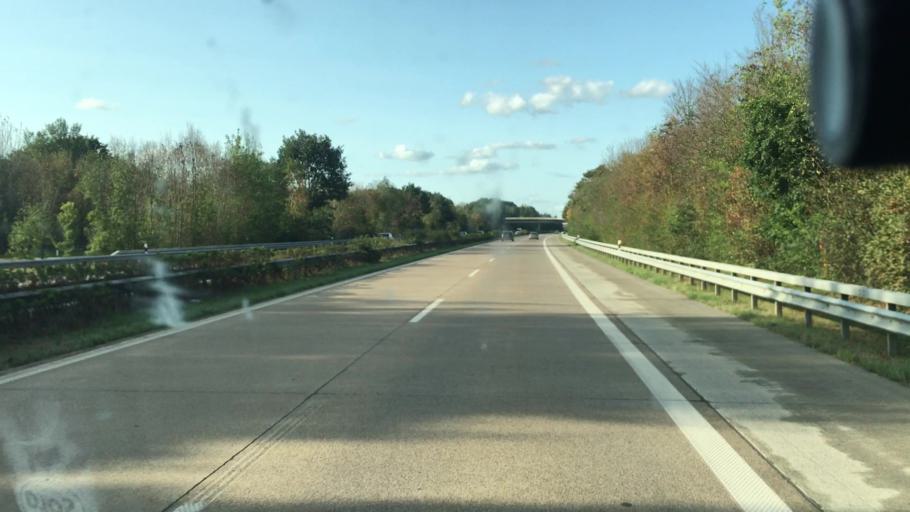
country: DE
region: Lower Saxony
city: Wiefelstede
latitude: 53.2944
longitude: 8.1474
